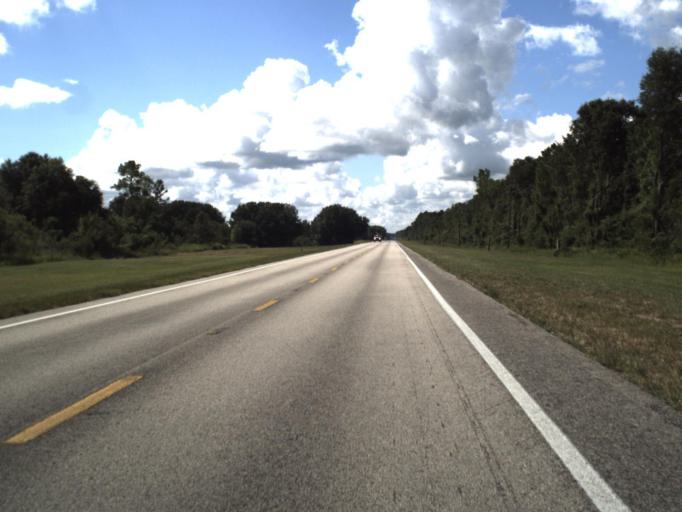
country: US
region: Florida
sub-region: Pasco County
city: Zephyrhills North
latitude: 28.2879
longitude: -82.0555
